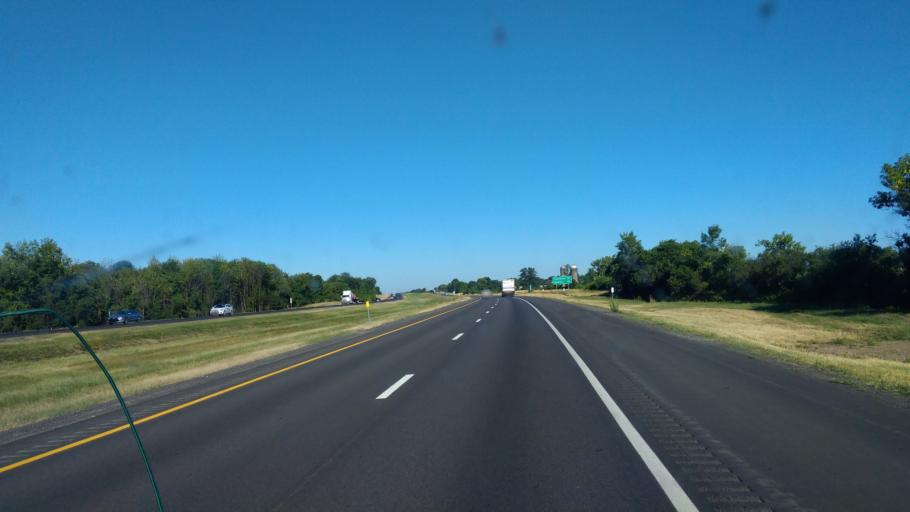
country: US
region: New York
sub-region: Ontario County
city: Phelps
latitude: 42.9742
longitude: -77.0903
